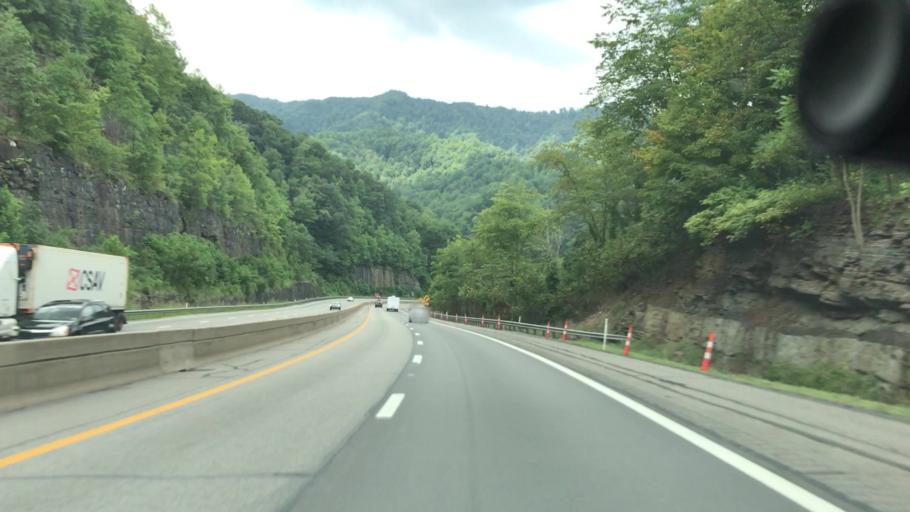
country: US
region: West Virginia
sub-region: Fayette County
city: Oak Hill
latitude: 37.9908
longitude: -81.3255
